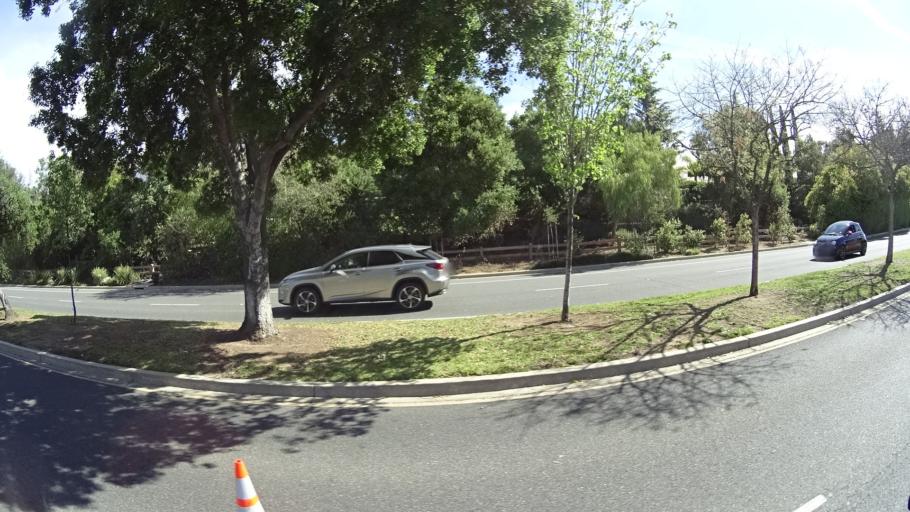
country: US
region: California
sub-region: Ventura County
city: Thousand Oaks
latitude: 34.1973
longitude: -118.8105
